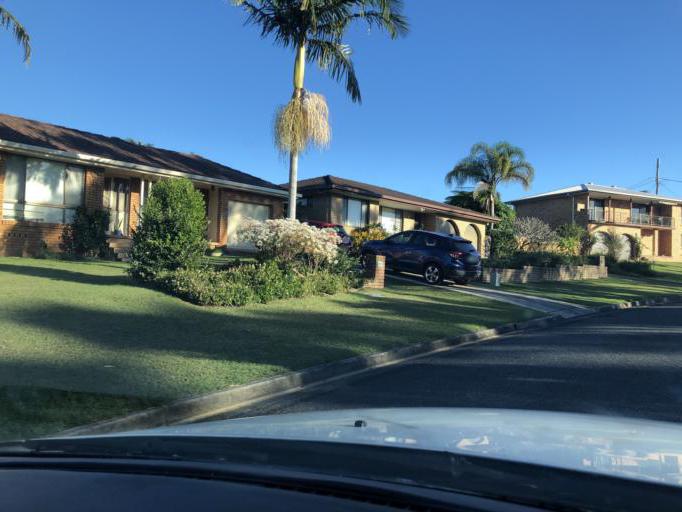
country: AU
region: New South Wales
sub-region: Coffs Harbour
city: Coffs Harbour
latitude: -30.2997
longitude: 153.1300
